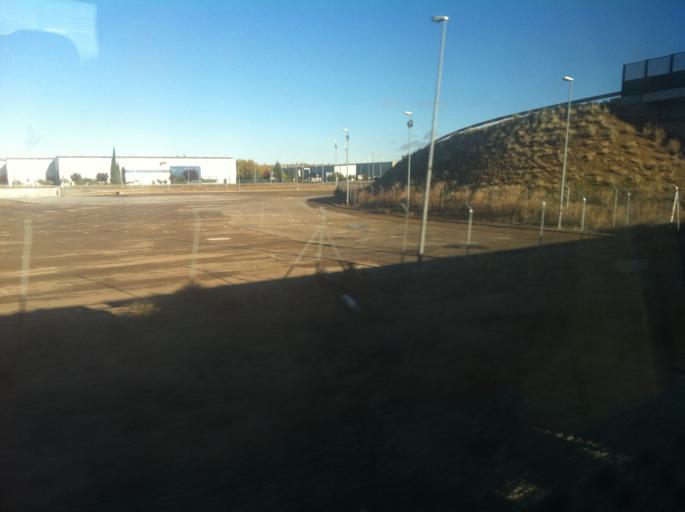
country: ES
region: Castille and Leon
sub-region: Provincia de Palencia
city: Venta de Banos
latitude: 41.9279
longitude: -4.4837
